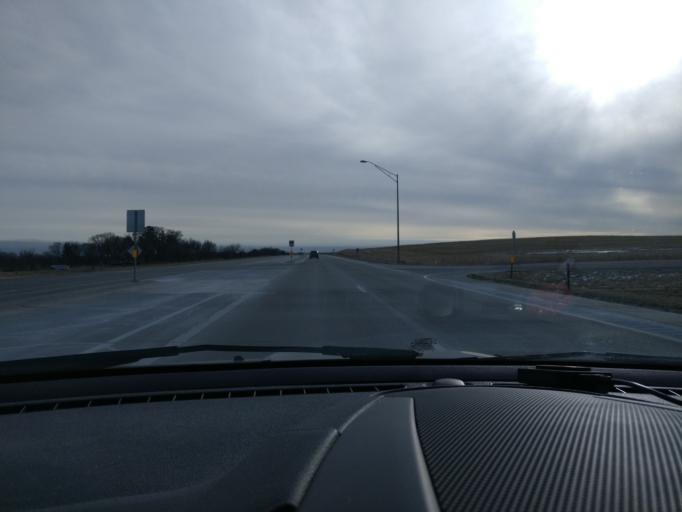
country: US
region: Nebraska
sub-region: Saunders County
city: Wahoo
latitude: 41.2202
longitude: -96.6374
